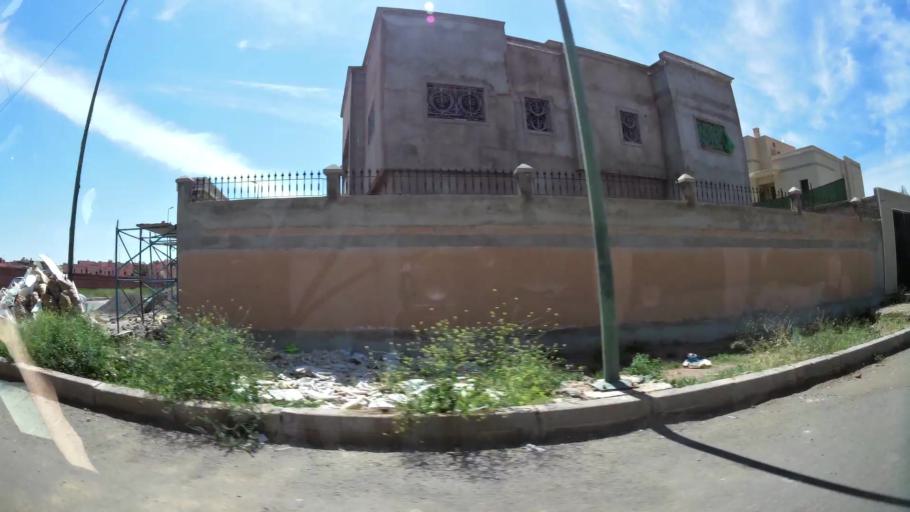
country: MA
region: Marrakech-Tensift-Al Haouz
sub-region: Marrakech
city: Marrakesh
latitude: 31.6495
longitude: -8.0705
